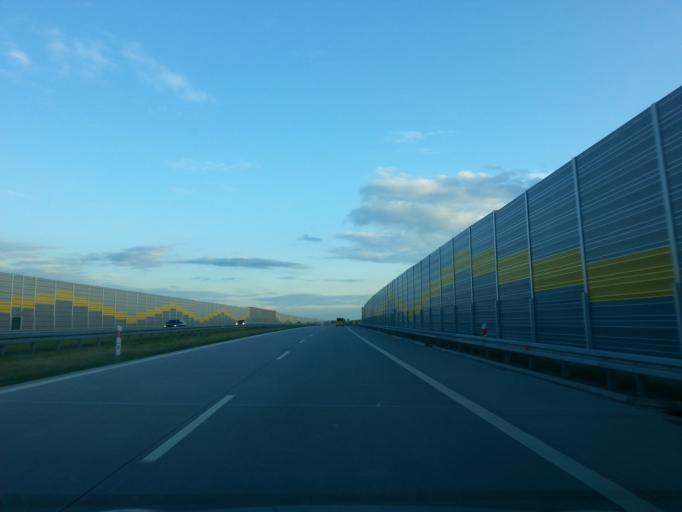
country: PL
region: Lodz Voivodeship
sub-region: Powiat sieradzki
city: Zloczew
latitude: 51.4221
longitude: 18.6443
